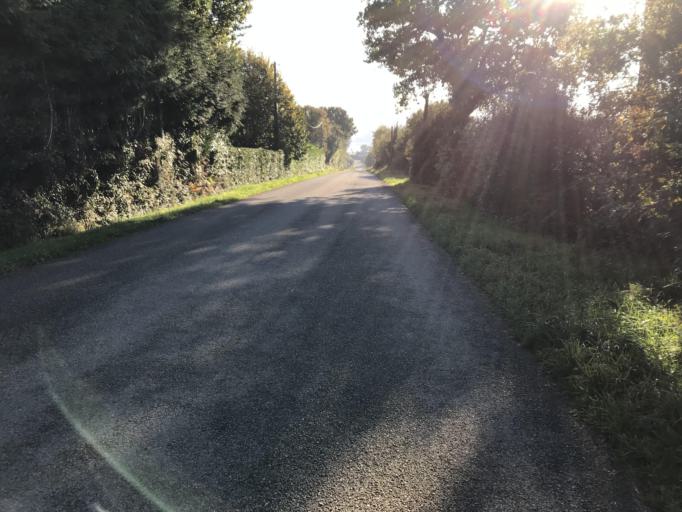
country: FR
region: Brittany
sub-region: Departement du Finistere
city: Hopital-Camfrout
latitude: 48.3061
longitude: -4.2322
